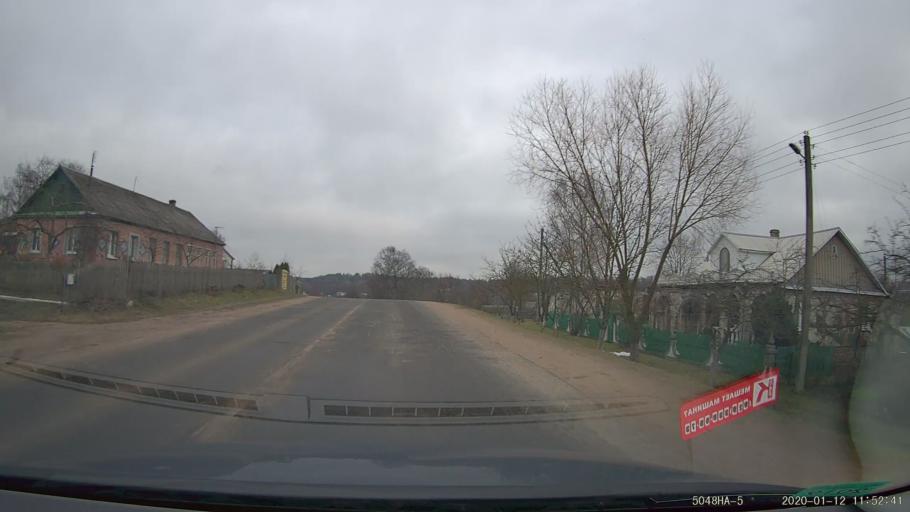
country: BY
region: Minsk
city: Rakaw
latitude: 53.9692
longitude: 27.1239
